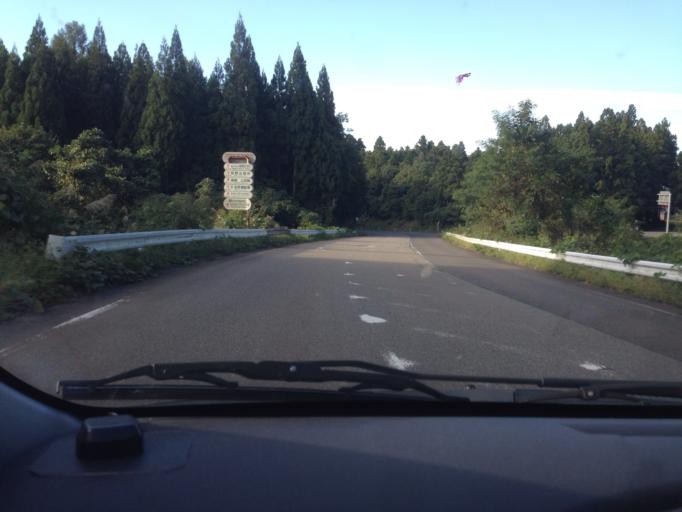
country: JP
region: Fukushima
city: Kitakata
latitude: 37.5948
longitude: 139.7620
